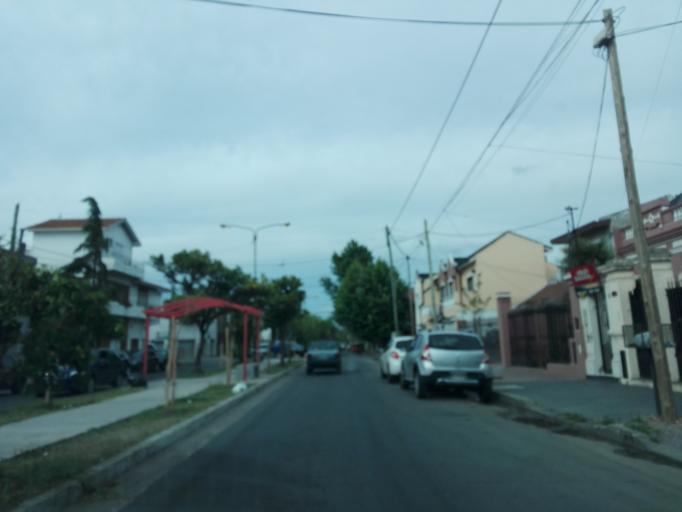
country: AR
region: Buenos Aires
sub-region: Partido de Lanus
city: Lanus
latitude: -34.7137
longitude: -58.3795
